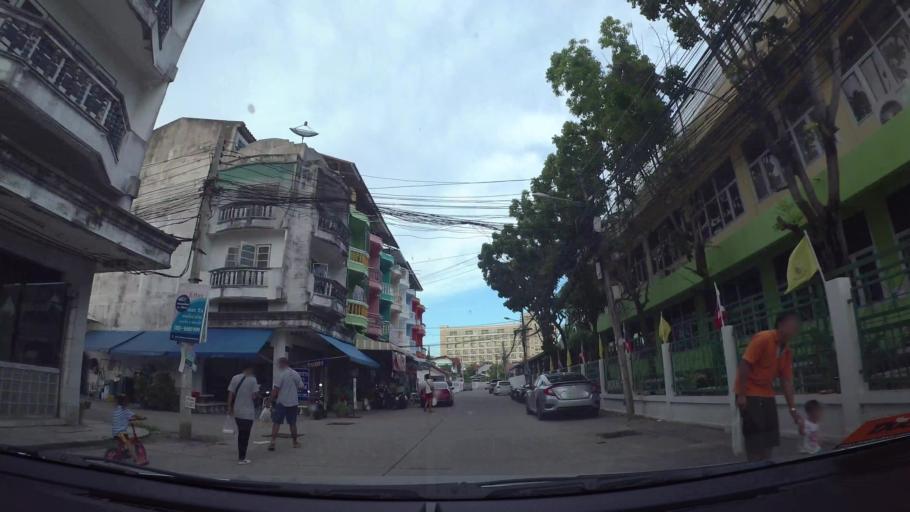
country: TH
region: Chon Buri
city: Phatthaya
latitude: 12.9138
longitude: 100.8822
